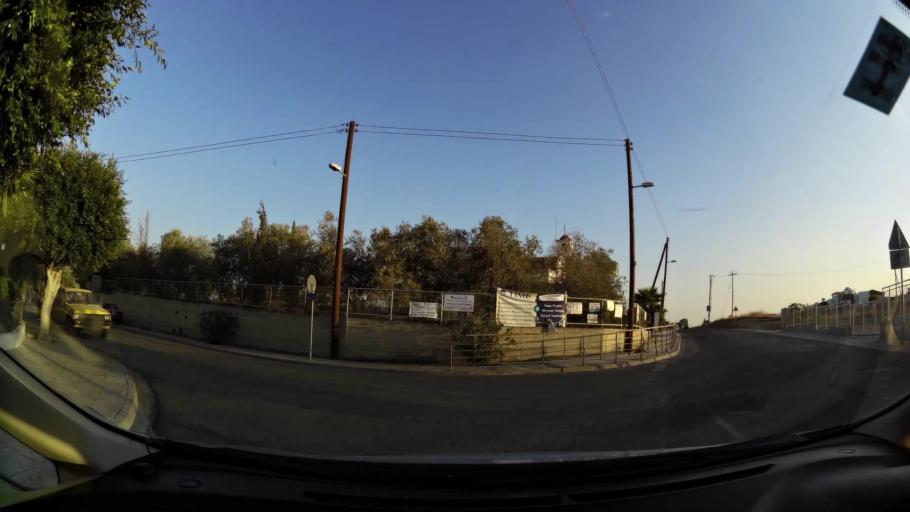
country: CY
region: Larnaka
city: Larnaca
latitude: 34.9158
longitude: 33.5905
